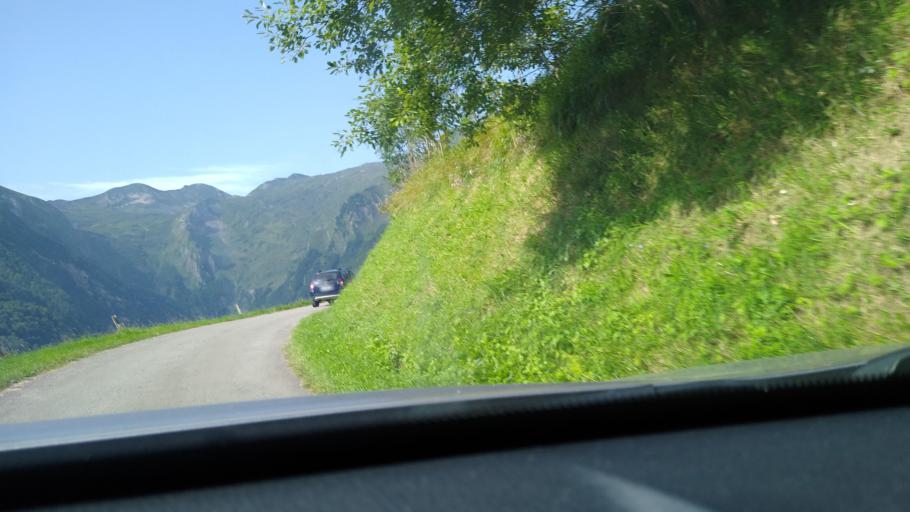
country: FR
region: Midi-Pyrenees
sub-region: Departement de l'Ariege
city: Saint-Girons
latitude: 42.7914
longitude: 1.1694
